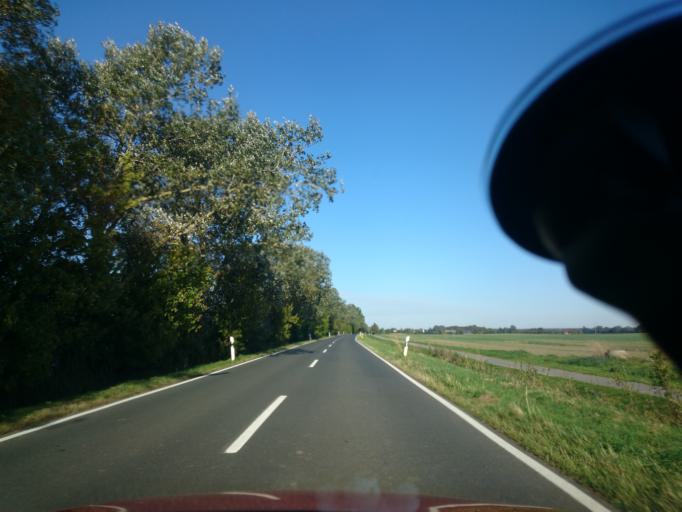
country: DE
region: Mecklenburg-Vorpommern
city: Saal
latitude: 54.3238
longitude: 12.5091
